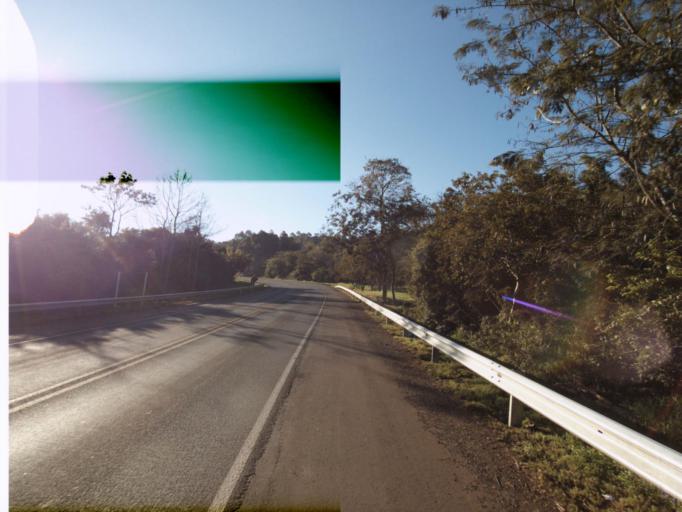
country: BR
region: Santa Catarina
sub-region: Chapeco
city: Chapeco
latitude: -26.9238
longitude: -52.8572
